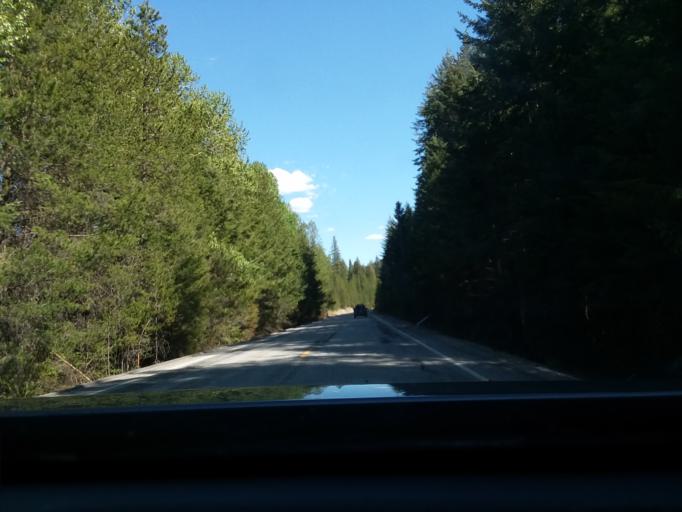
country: US
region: Washington
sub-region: Chelan County
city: Leavenworth
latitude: 47.7971
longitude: -120.6668
